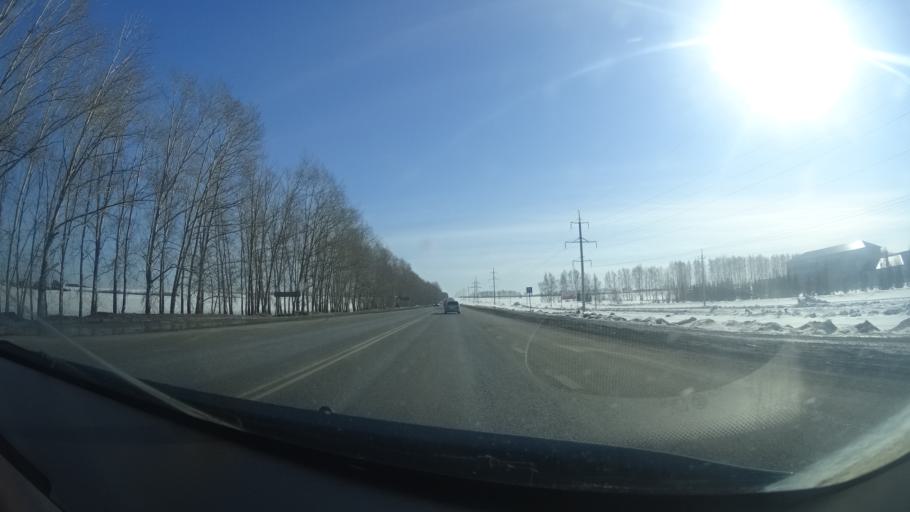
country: RU
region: Bashkortostan
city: Mikhaylovka
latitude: 54.8632
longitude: 55.7515
